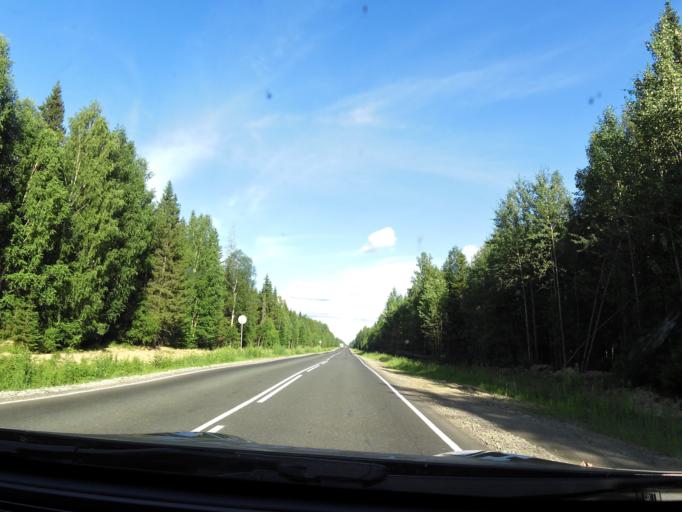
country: RU
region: Kirov
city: Chernaya Kholunitsa
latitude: 58.7757
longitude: 51.9284
